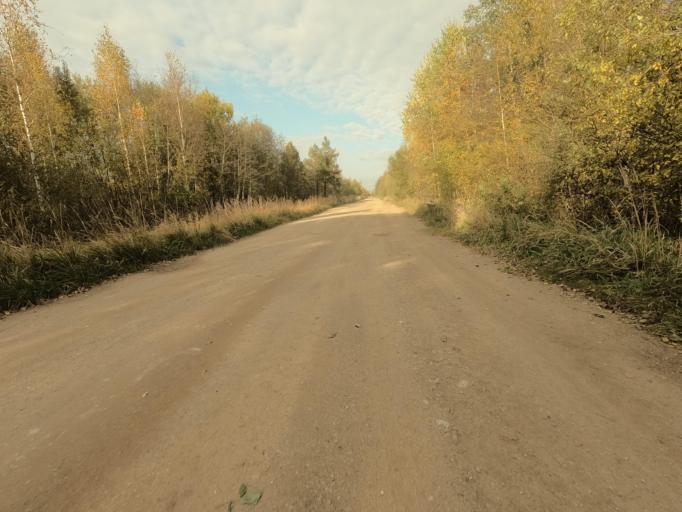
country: RU
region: Novgorod
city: Volkhovskiy
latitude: 58.9002
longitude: 31.0328
